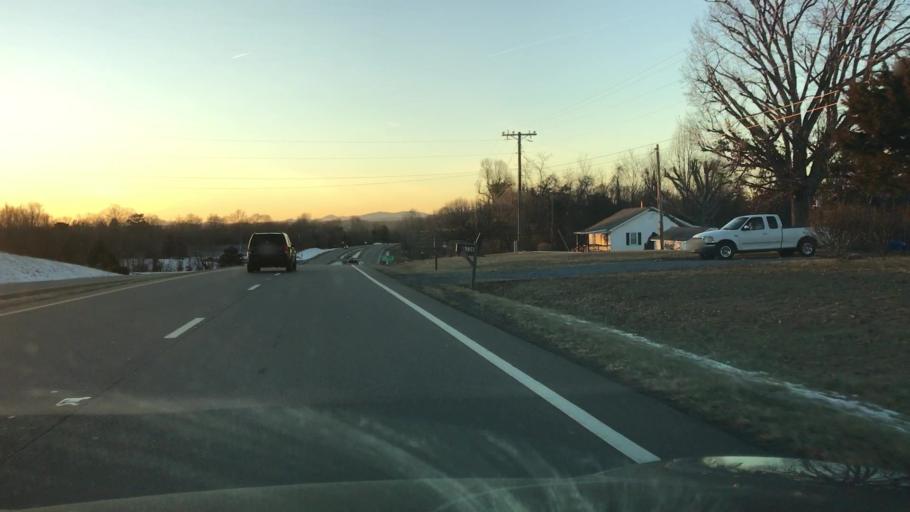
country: US
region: Virginia
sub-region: Bedford County
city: Forest
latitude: 37.3006
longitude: -79.3708
